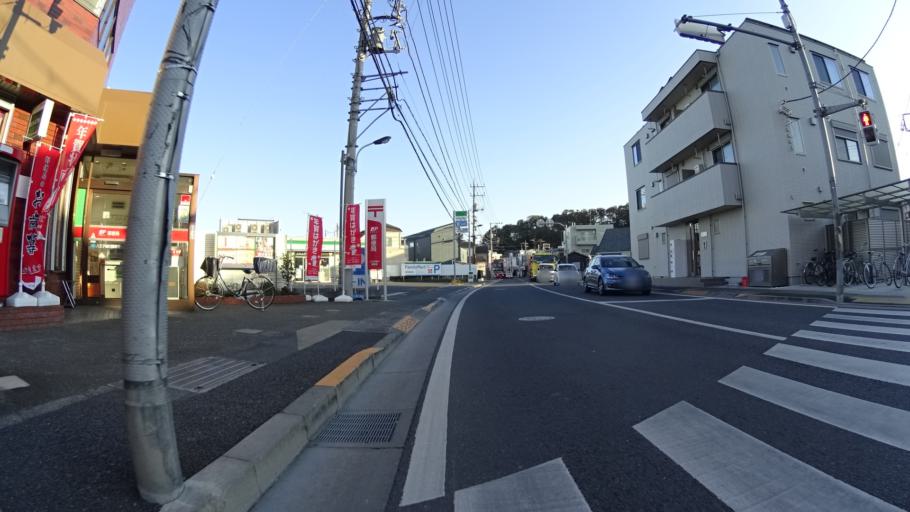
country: JP
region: Tokyo
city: Hachioji
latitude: 35.6653
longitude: 139.3042
